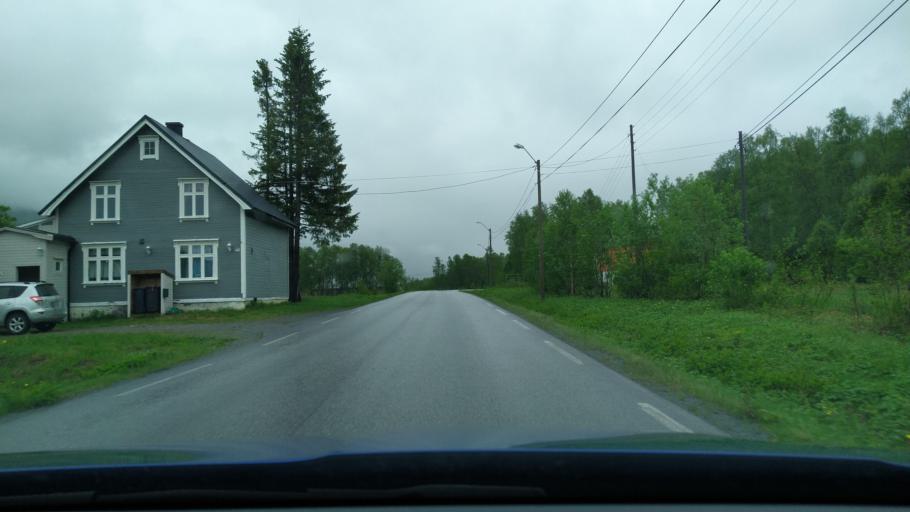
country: NO
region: Troms
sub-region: Dyroy
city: Brostadbotn
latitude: 69.0543
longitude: 17.7316
